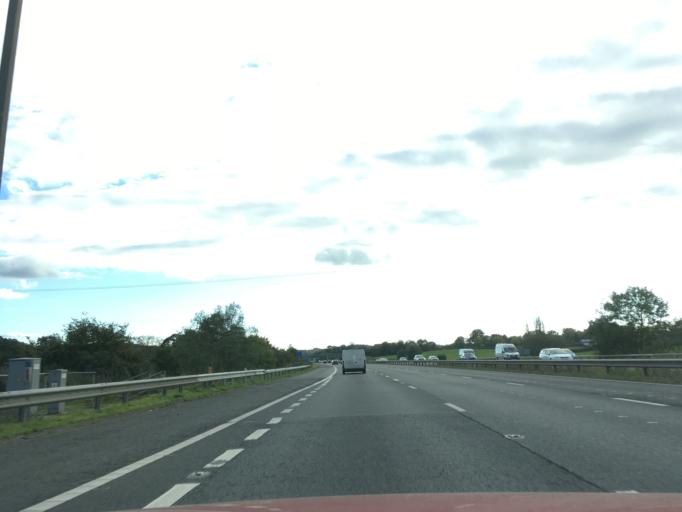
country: GB
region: England
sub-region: South Gloucestershire
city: Falfield
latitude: 51.6330
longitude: -2.4560
